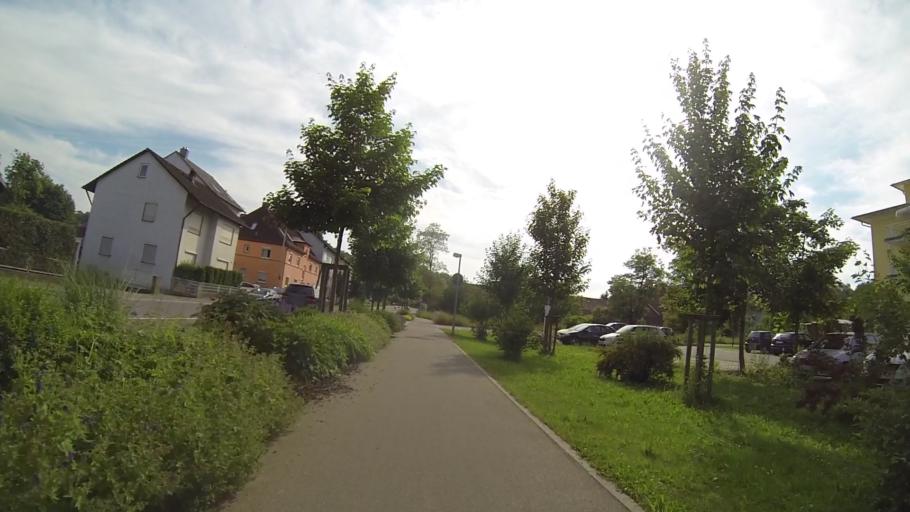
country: DE
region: Bavaria
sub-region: Swabia
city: Senden
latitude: 48.3248
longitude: 10.0293
